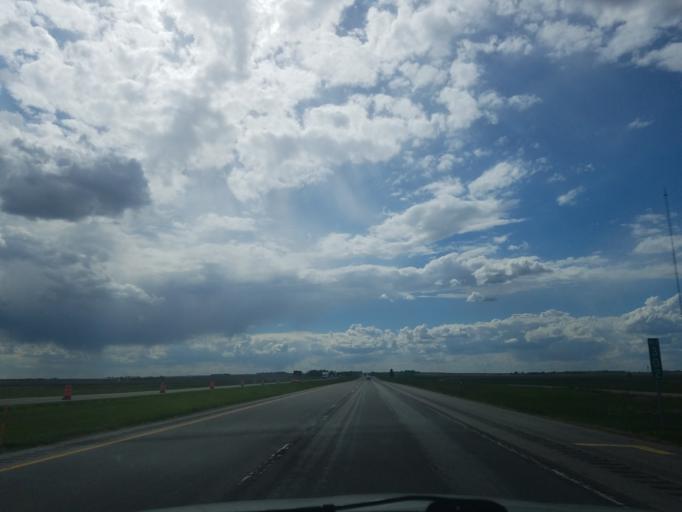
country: US
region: North Dakota
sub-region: Barnes County
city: Valley City
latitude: 46.9201
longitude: -97.8018
